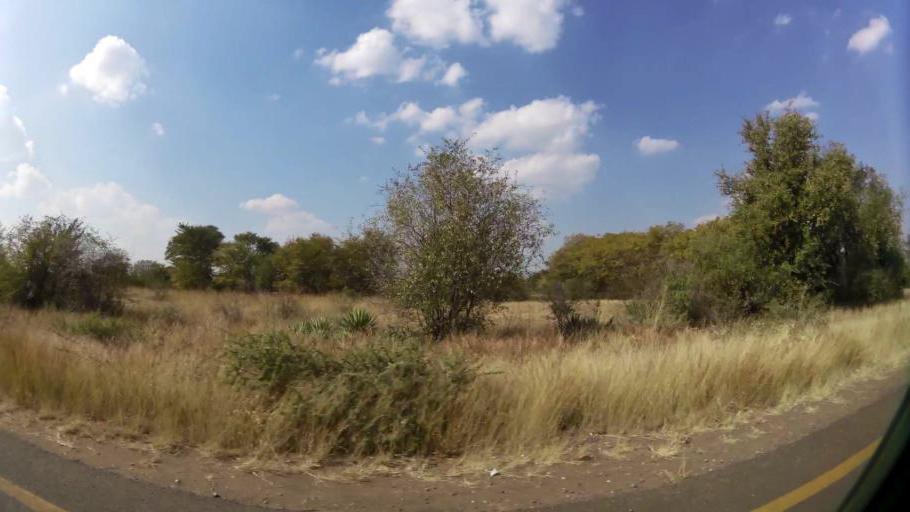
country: ZA
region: North-West
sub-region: Bojanala Platinum District Municipality
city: Mogwase
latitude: -25.4563
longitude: 27.0877
